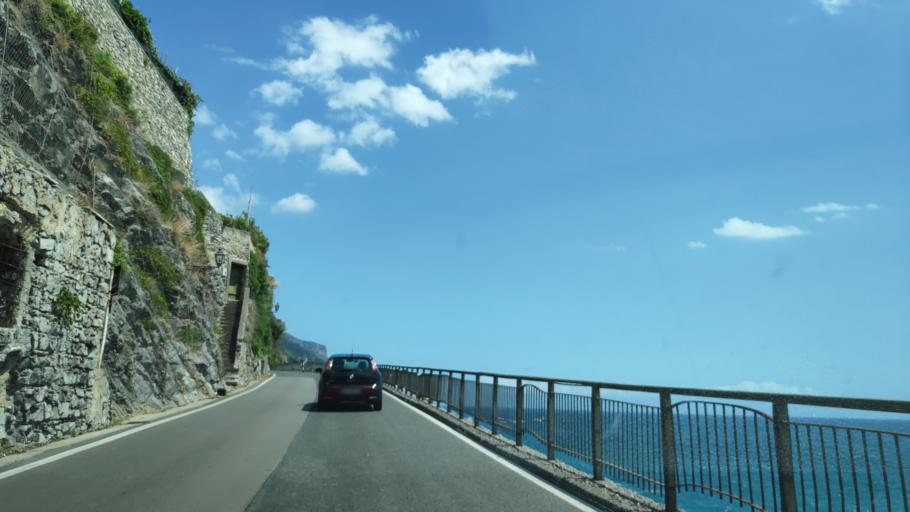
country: IT
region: Campania
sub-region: Provincia di Salerno
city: Minori
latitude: 40.6485
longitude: 14.6300
